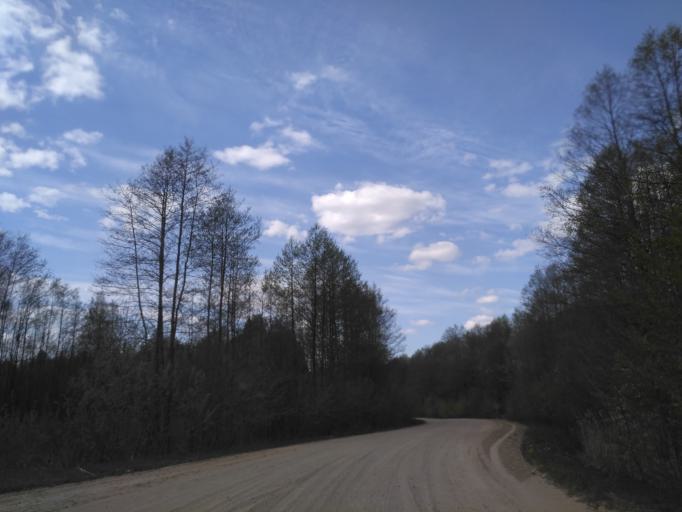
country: BY
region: Minsk
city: Narach
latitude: 54.9965
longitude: 26.5582
